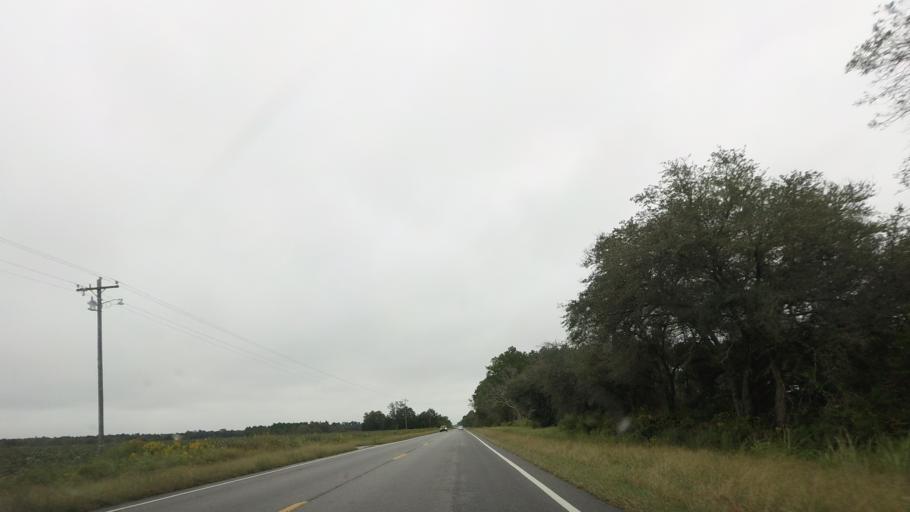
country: US
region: Georgia
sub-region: Berrien County
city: Nashville
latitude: 31.3278
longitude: -83.2303
